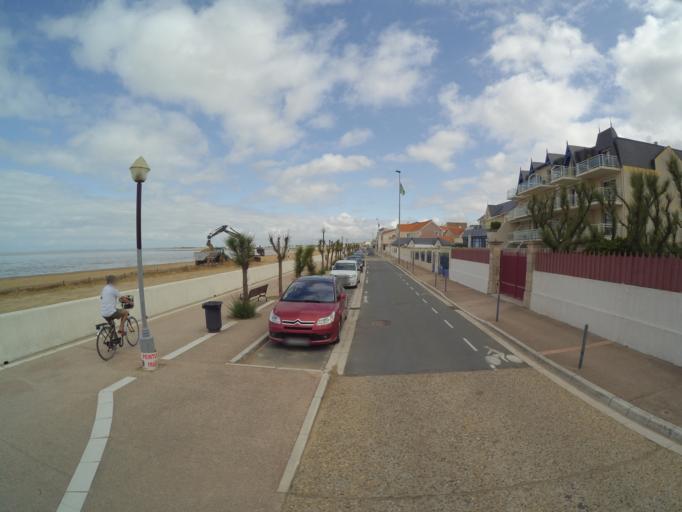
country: FR
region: Poitou-Charentes
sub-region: Departement de la Charente-Maritime
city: Chatelaillon-Plage
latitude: 46.0733
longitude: -1.0933
